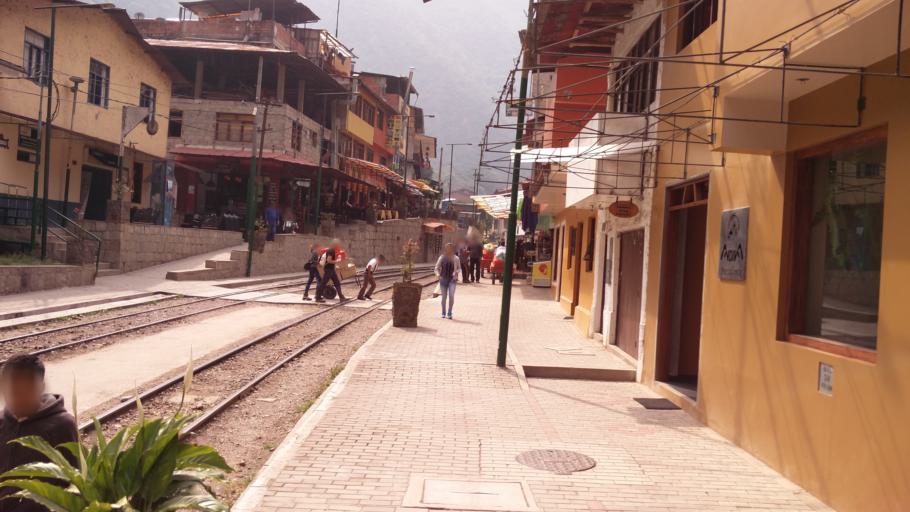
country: PE
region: Cusco
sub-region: Provincia de La Convencion
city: Santa Teresa
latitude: -13.1543
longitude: -72.5264
